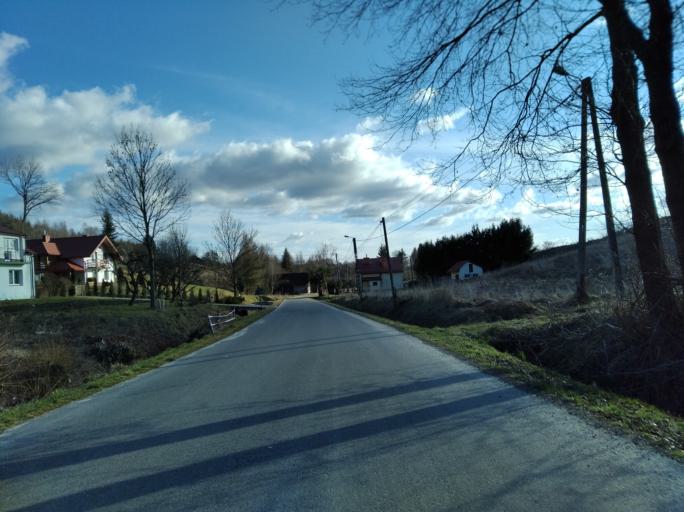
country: PL
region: Subcarpathian Voivodeship
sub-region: Powiat strzyzowski
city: Wisniowa
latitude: 49.8905
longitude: 21.7134
